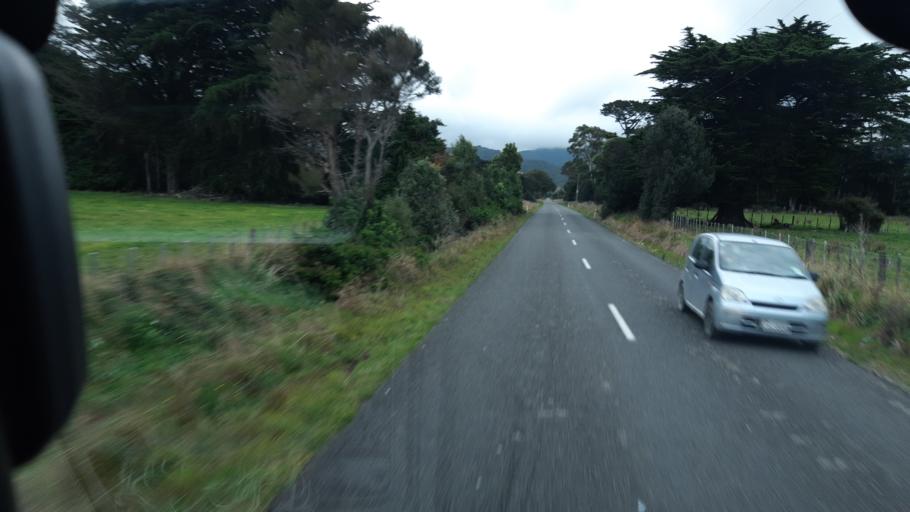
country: NZ
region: Manawatu-Wanganui
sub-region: Palmerston North City
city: Palmerston North
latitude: -40.5762
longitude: 175.6534
